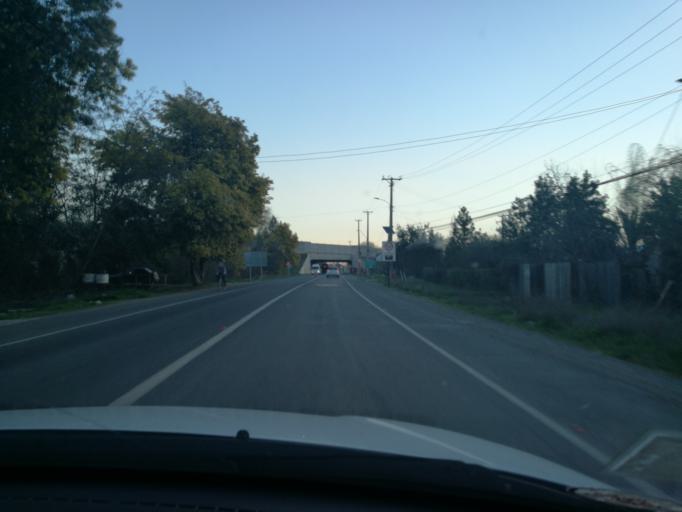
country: CL
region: O'Higgins
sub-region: Provincia de Cachapoal
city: Graneros
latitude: -34.0423
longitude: -70.7243
